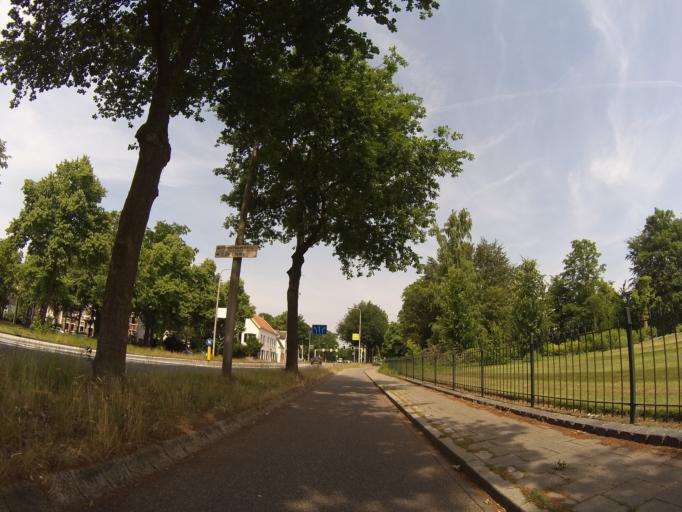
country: NL
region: Utrecht
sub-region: Gemeente Zeist
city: Zeist
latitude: 52.0879
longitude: 5.2302
